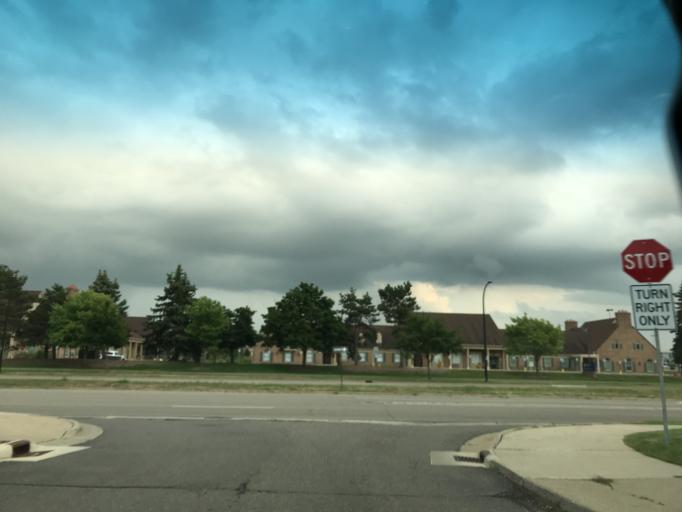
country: US
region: Michigan
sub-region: Washtenaw County
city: Ann Arbor
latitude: 42.2442
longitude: -83.7426
